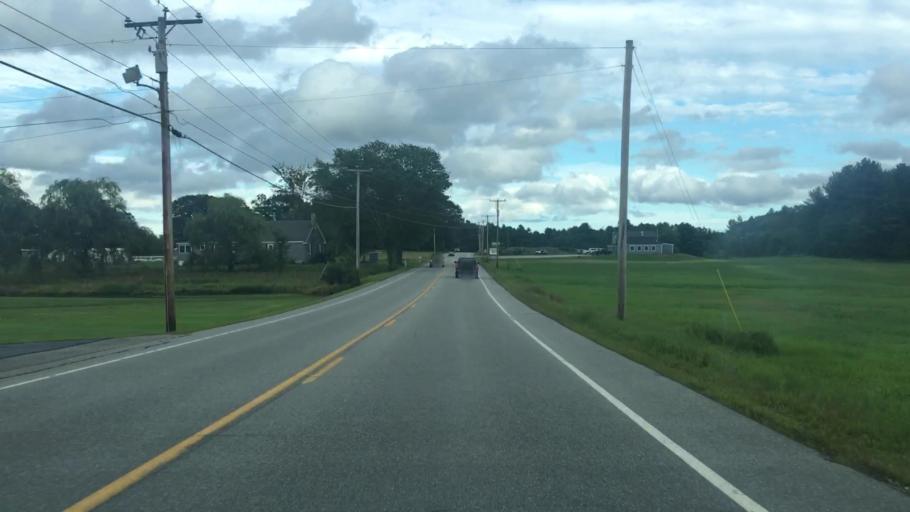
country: US
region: Maine
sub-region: York County
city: Dayton
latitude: 43.5438
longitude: -70.5288
